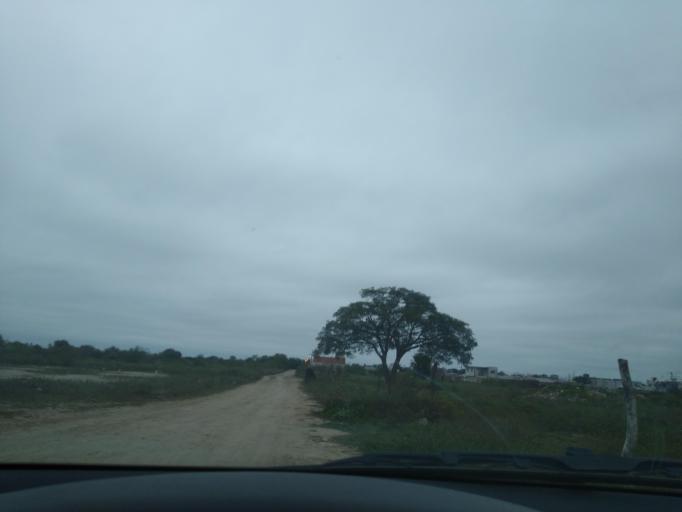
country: AR
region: Chaco
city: Fontana
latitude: -27.4016
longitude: -58.9815
